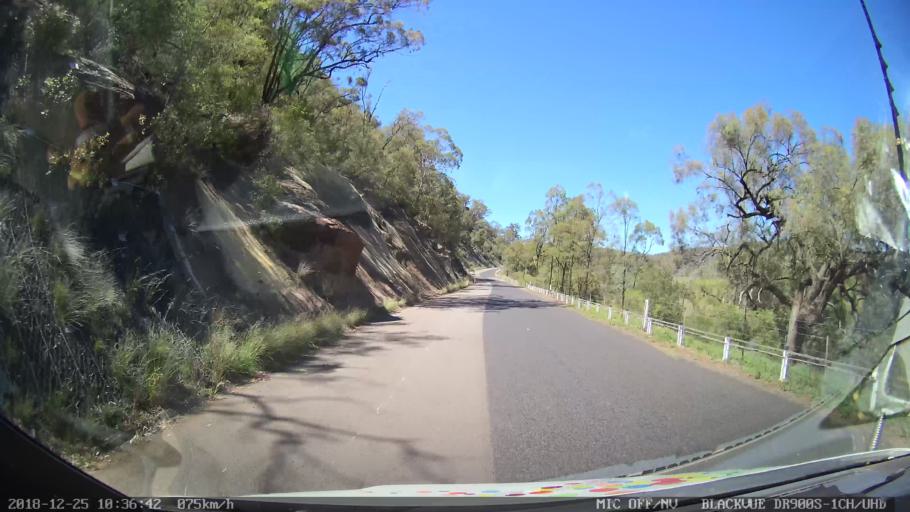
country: AU
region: New South Wales
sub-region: Upper Hunter Shire
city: Merriwa
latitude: -32.4065
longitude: 150.3837
